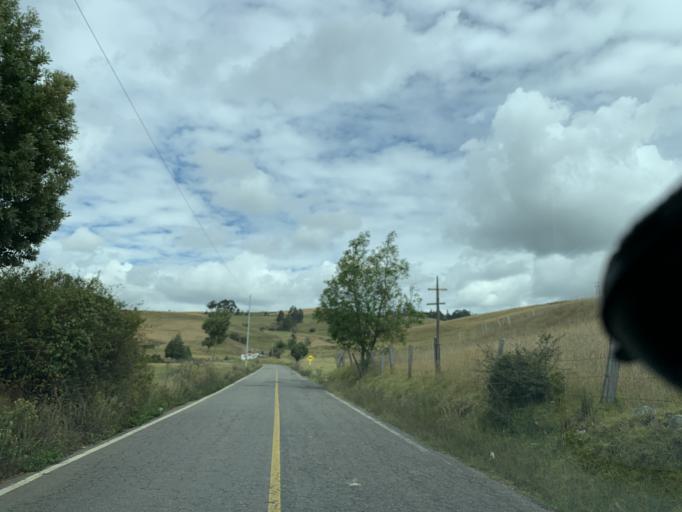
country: CO
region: Boyaca
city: Toca
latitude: 5.5722
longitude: -73.2329
